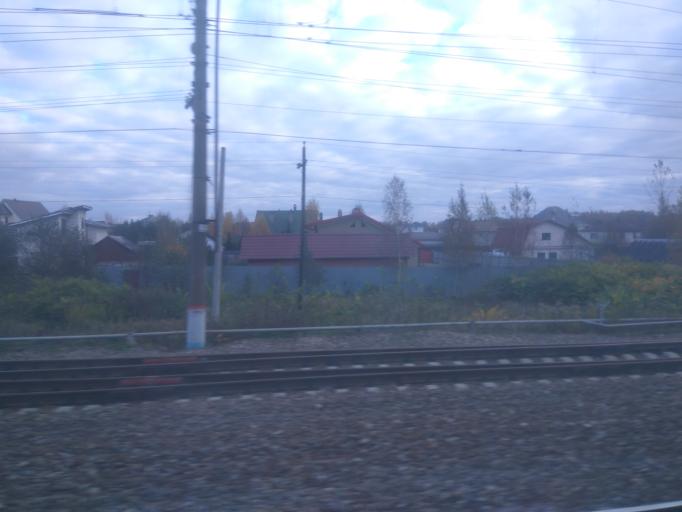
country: RU
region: Moskovskaya
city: Kokoshkino
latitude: 55.6041
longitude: 37.1793
